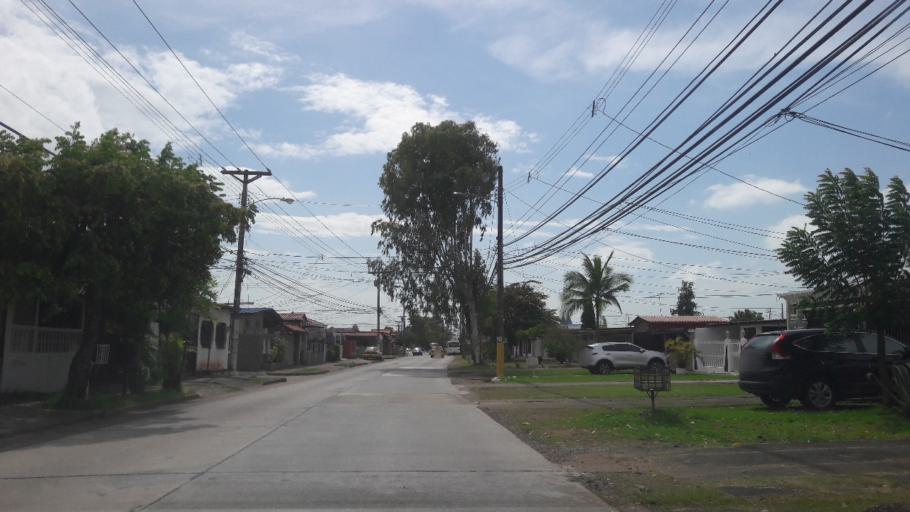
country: PA
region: Panama
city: Tocumen
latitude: 9.0585
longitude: -79.4191
